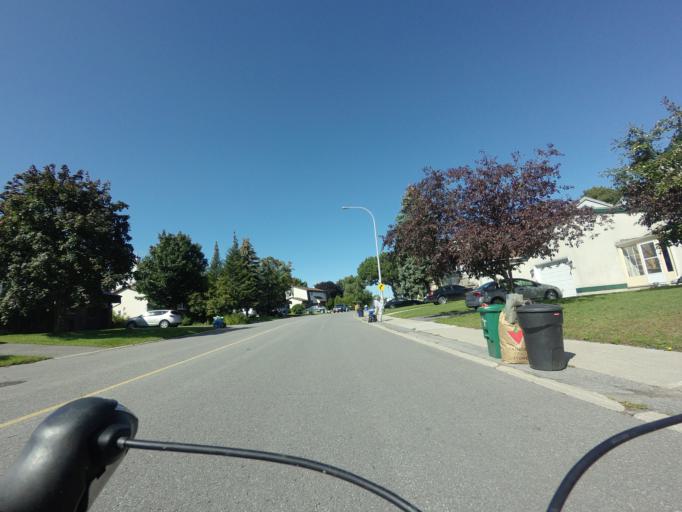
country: CA
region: Ontario
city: Bells Corners
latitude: 45.3164
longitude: -75.8387
